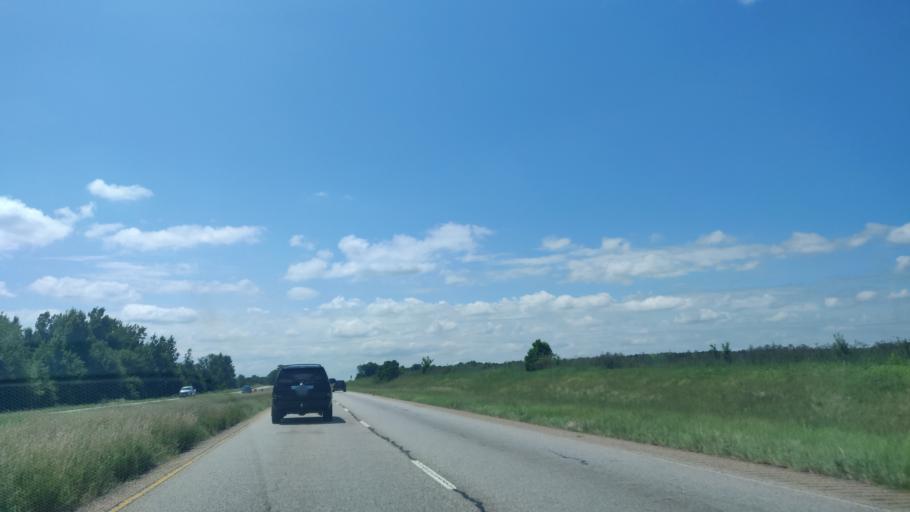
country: US
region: Georgia
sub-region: Stewart County
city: Richland
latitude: 32.0771
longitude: -84.6734
